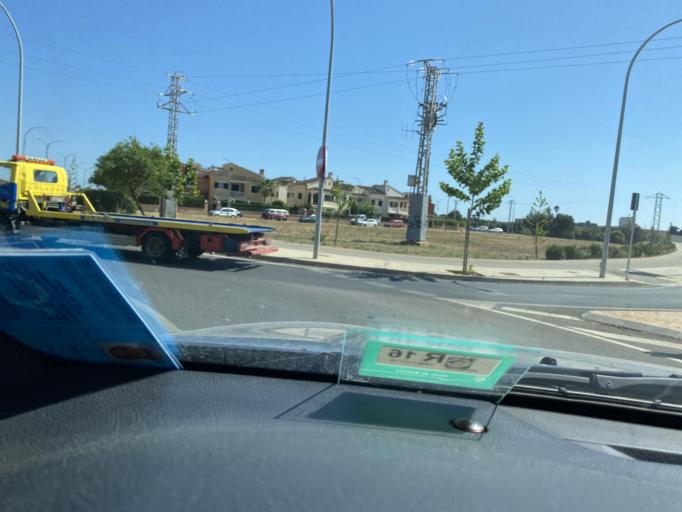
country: ES
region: Balearic Islands
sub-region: Illes Balears
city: Palma
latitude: 39.6140
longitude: 2.6834
